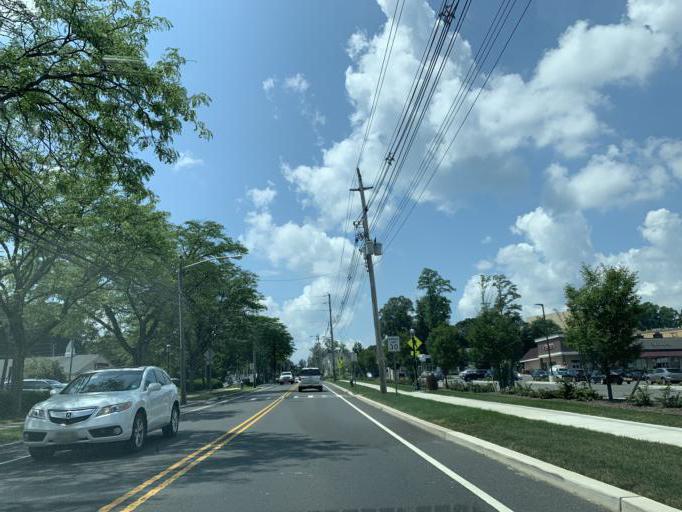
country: US
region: New Jersey
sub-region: Somerset County
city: Bernardsville
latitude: 40.7196
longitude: -74.5622
